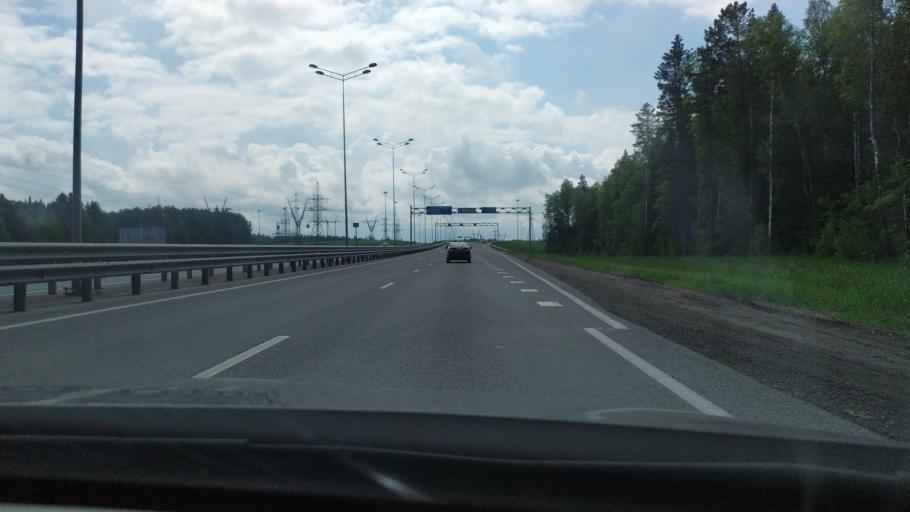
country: RU
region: Perm
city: Novyye Lyady
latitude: 58.0514
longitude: 56.4289
